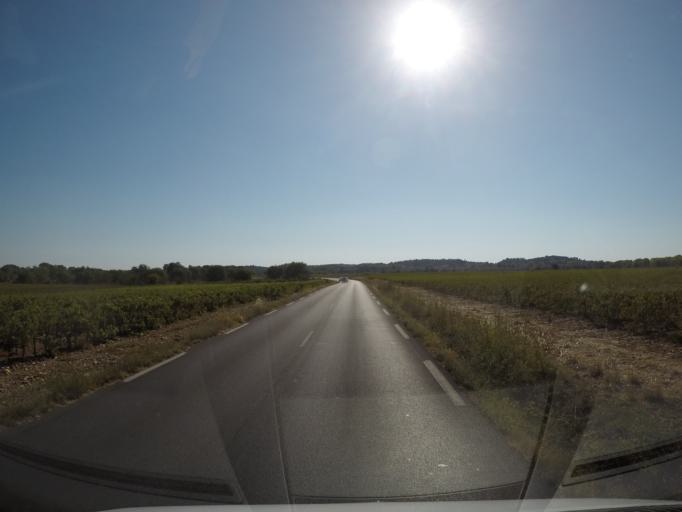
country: FR
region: Languedoc-Roussillon
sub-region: Departement du Gard
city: Lezan
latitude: 44.0230
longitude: 4.0382
